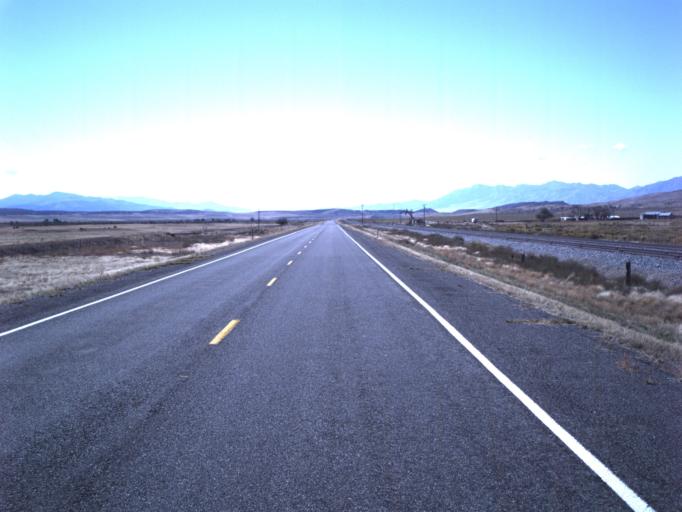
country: US
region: Utah
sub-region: Juab County
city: Nephi
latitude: 39.5232
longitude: -111.9375
